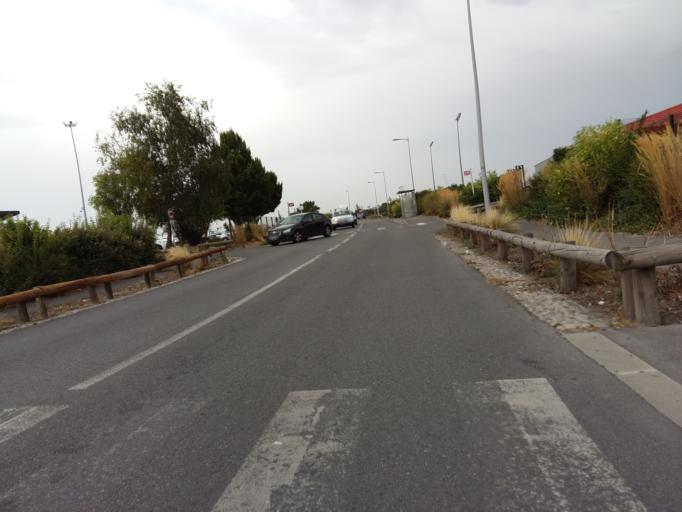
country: FR
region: Picardie
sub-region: Departement de la Somme
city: Camon
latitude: 49.8998
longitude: 2.3408
